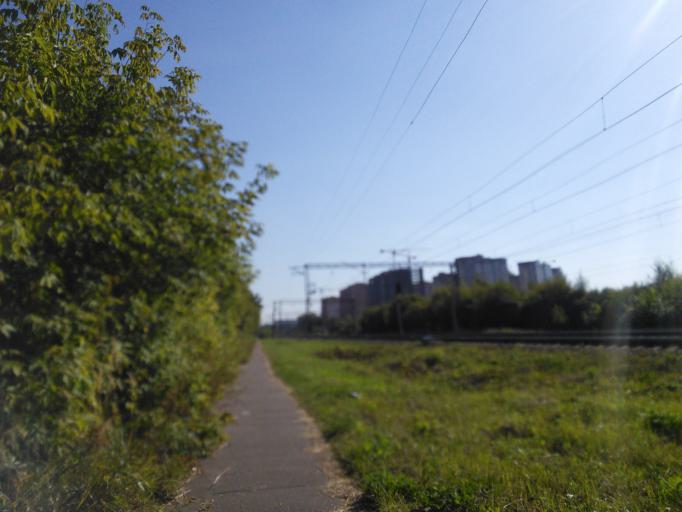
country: RU
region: Moskovskaya
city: Shcherbinka
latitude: 55.4994
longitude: 37.5594
